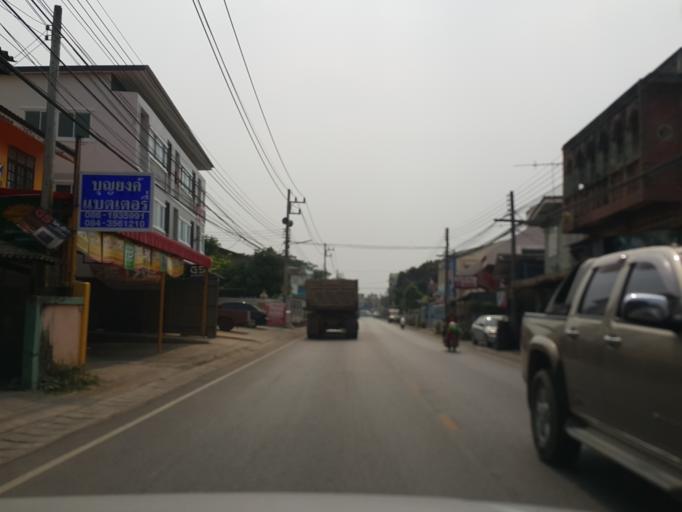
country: TH
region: Lampang
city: Ko Kha
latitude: 18.1937
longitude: 99.3938
